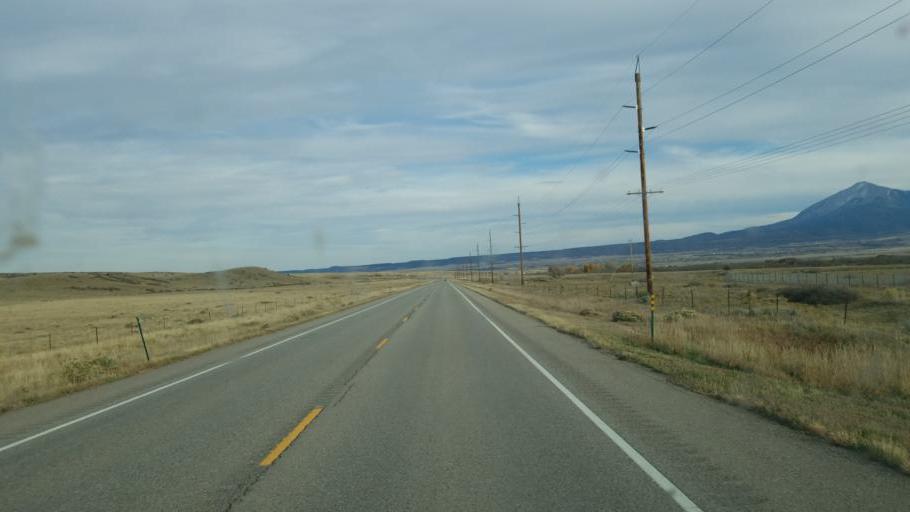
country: US
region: Colorado
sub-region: Huerfano County
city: Walsenburg
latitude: 37.5446
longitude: -105.0817
